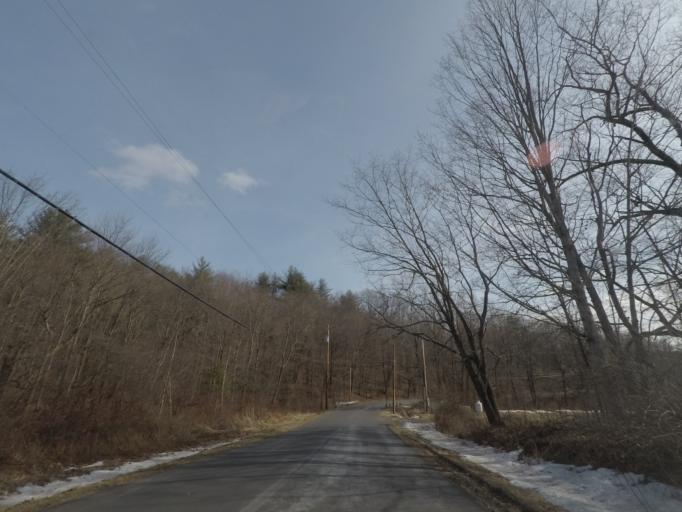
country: US
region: New York
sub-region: Rensselaer County
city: Nassau
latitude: 42.5043
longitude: -73.5520
